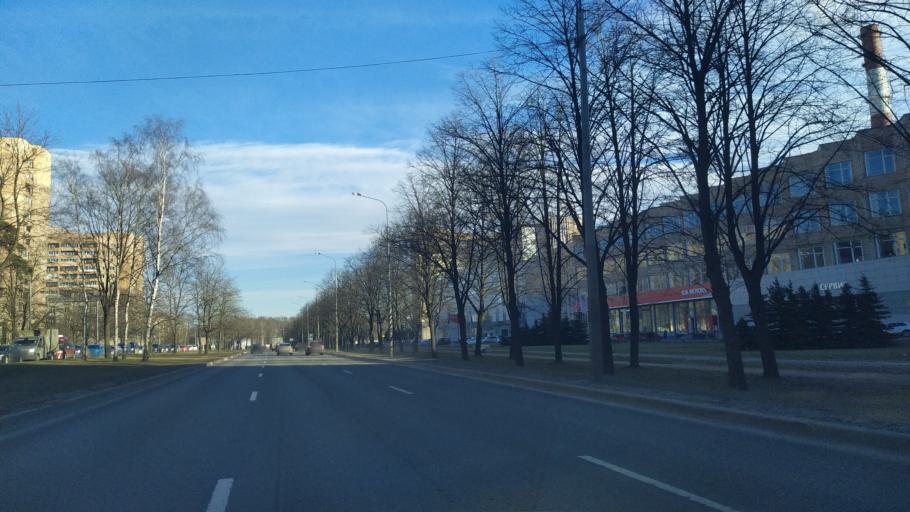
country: RU
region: Leningrad
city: Kalininskiy
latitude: 59.9955
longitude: 30.3842
